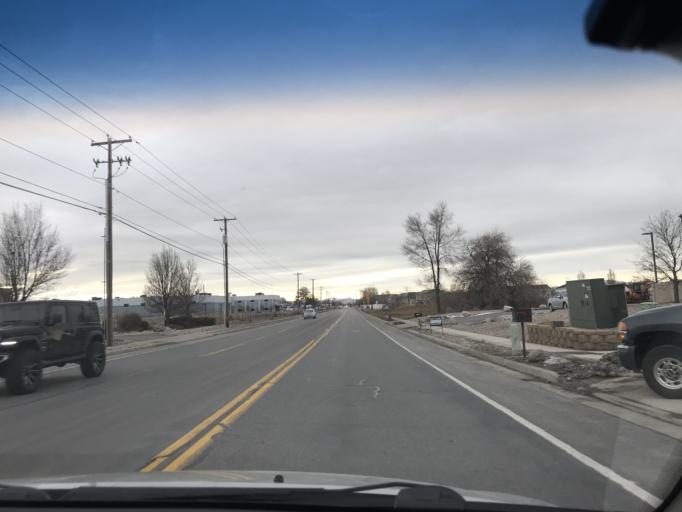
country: US
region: Utah
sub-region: Davis County
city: North Salt Lake
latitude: 40.8617
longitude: -111.9169
